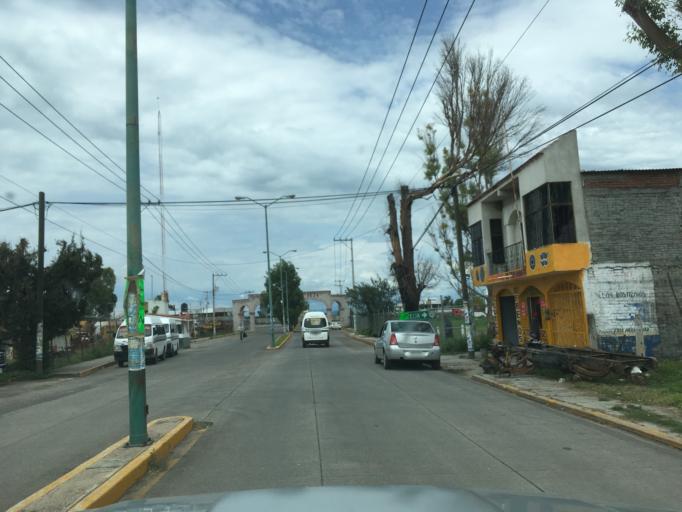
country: MX
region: Michoacan
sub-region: Tarimbaro
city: Meson Nuevo (Canada de la Magdalena)
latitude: 19.7970
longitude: -101.1644
